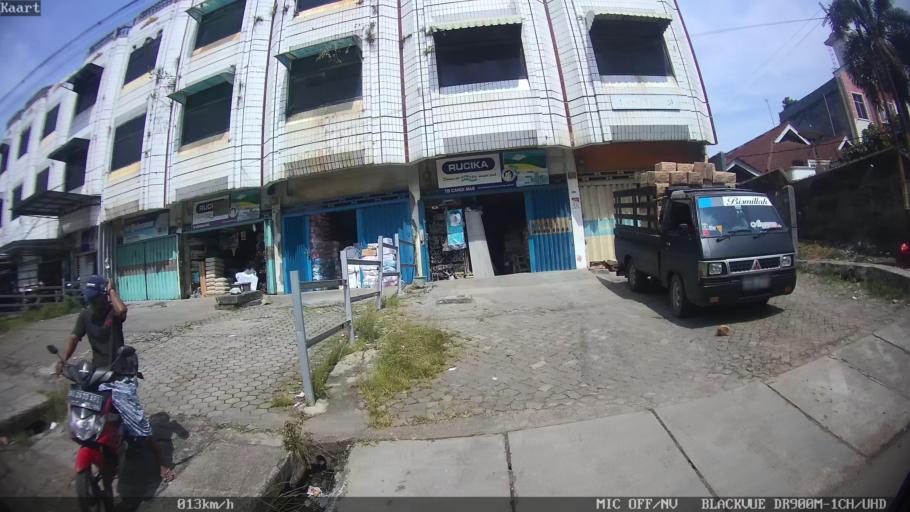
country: ID
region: Lampung
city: Kedaton
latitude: -5.3772
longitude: 105.2723
